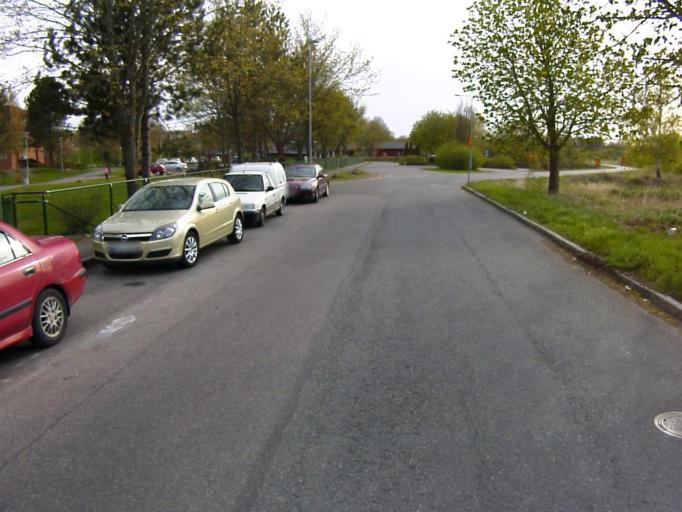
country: SE
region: Skane
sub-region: Kristianstads Kommun
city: Kristianstad
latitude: 56.0620
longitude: 14.1555
